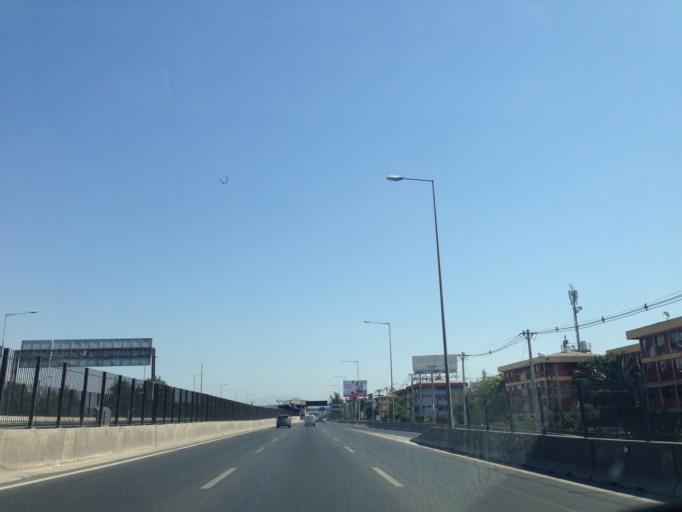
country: CL
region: Santiago Metropolitan
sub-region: Provincia de Santiago
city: Villa Presidente Frei, Nunoa, Santiago, Chile
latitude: -33.4761
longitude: -70.5781
